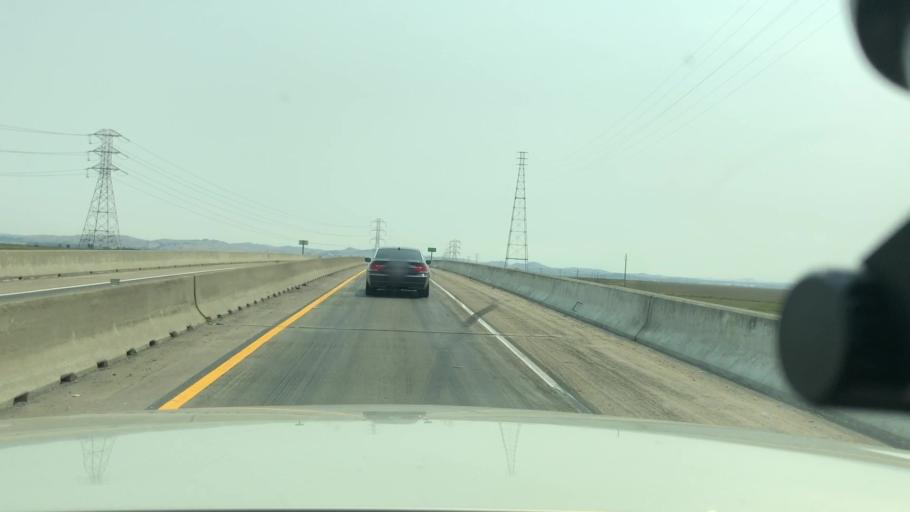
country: US
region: California
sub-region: Marin County
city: Black Point-Green Point
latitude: 38.1557
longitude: -122.4082
